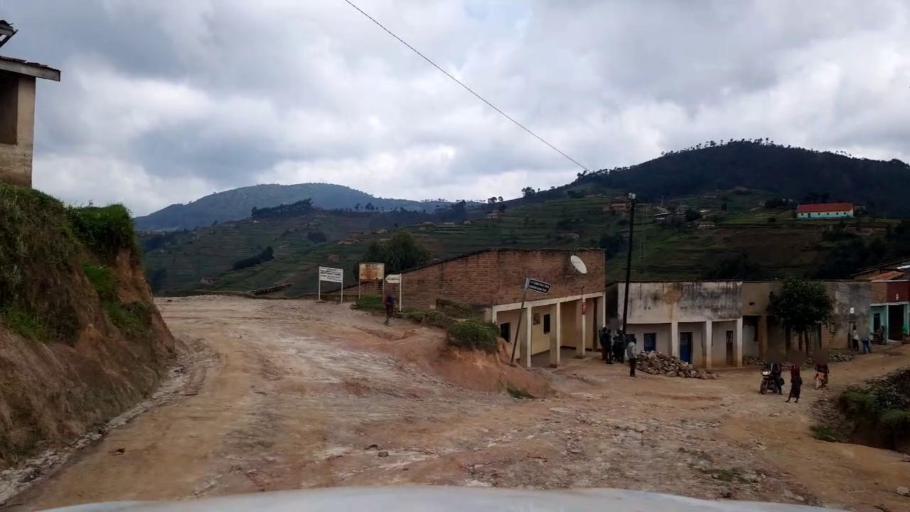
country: RW
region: Western Province
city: Kibuye
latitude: -1.9477
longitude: 29.4725
